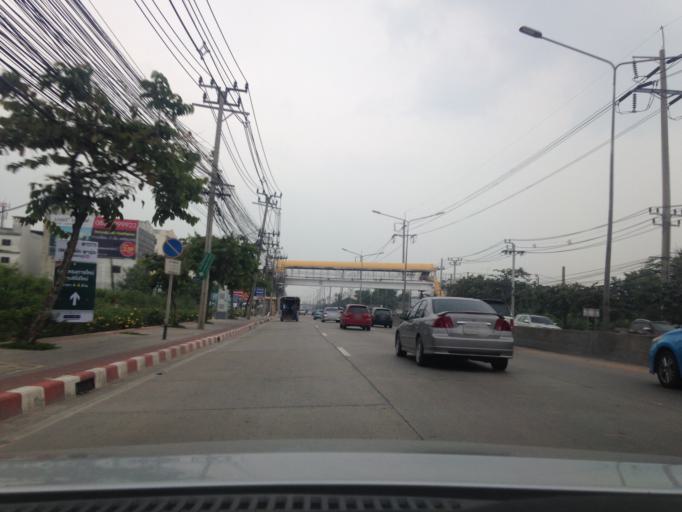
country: TH
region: Bangkok
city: Lat Krabang
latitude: 13.7331
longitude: 100.7464
